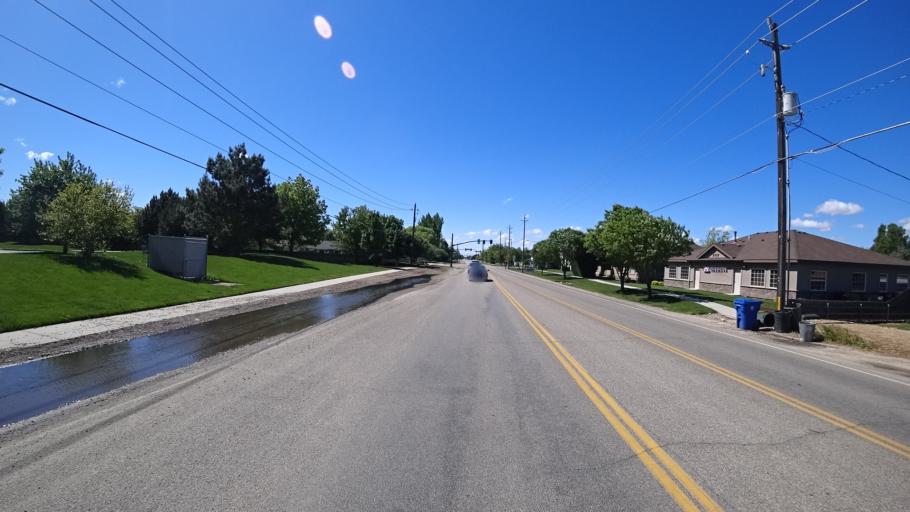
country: US
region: Idaho
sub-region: Ada County
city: Meridian
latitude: 43.6390
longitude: -116.3745
